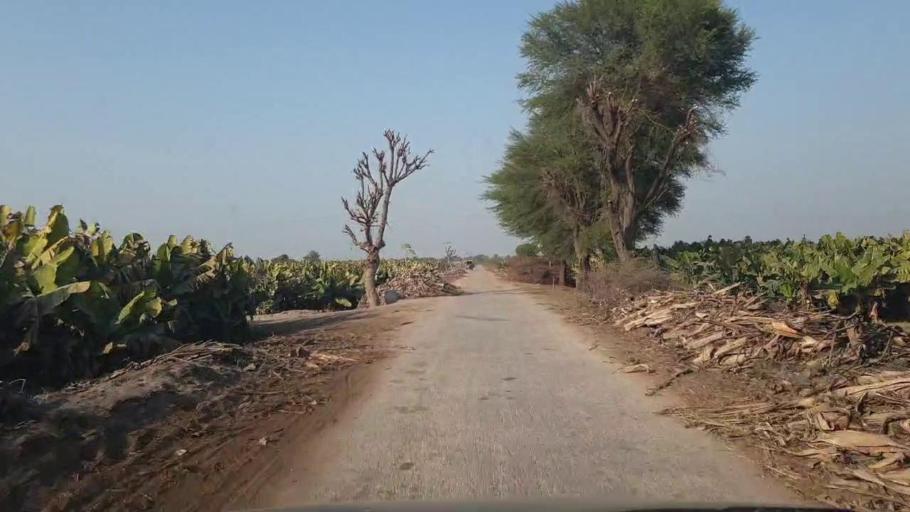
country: PK
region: Sindh
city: Bhit Shah
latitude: 25.8178
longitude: 68.5139
